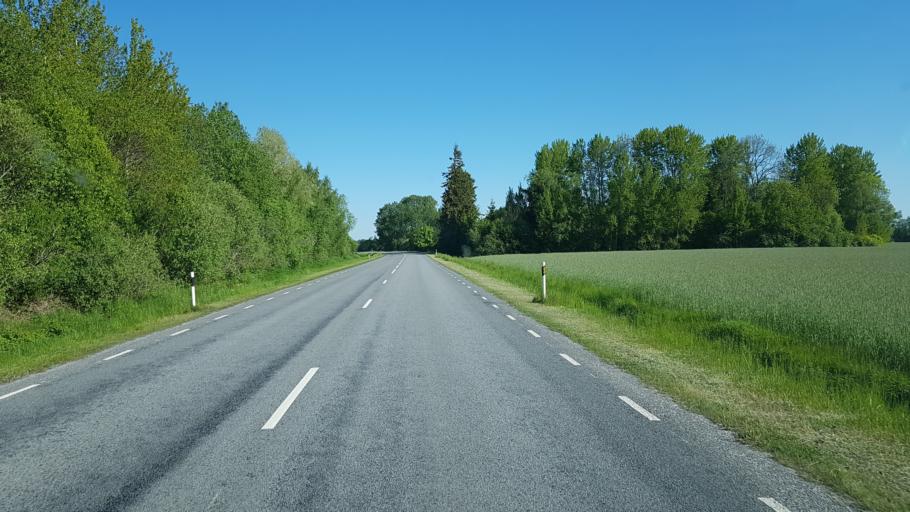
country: EE
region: Laeaene
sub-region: Ridala Parish
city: Uuemoisa
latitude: 58.8537
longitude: 23.6383
